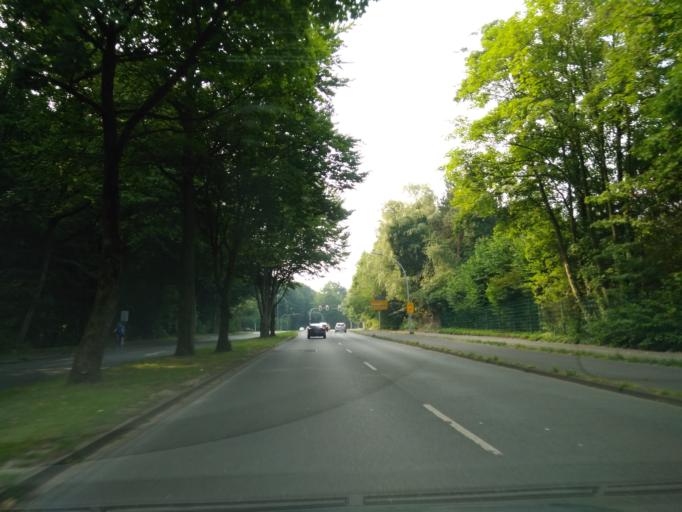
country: DE
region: North Rhine-Westphalia
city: Marl
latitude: 51.5847
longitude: 7.0646
